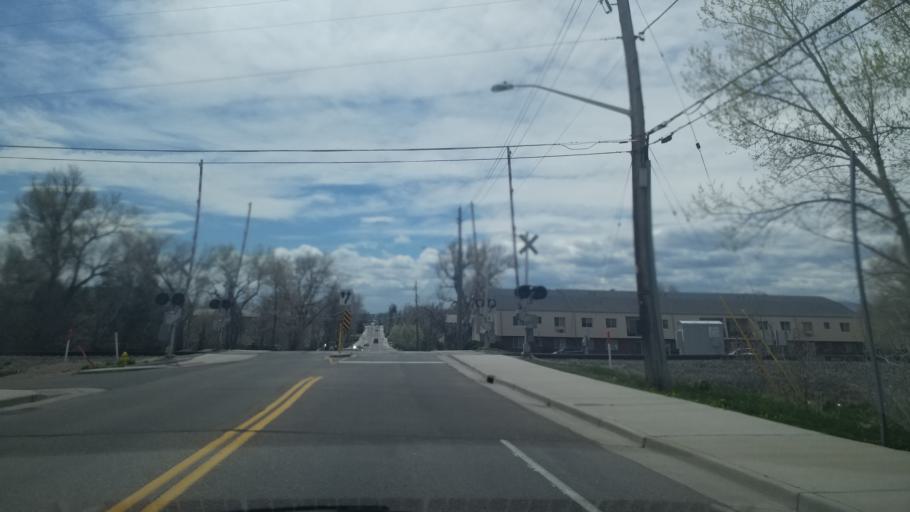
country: US
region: Colorado
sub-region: Jefferson County
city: Arvada
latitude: 39.8077
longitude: -105.0814
